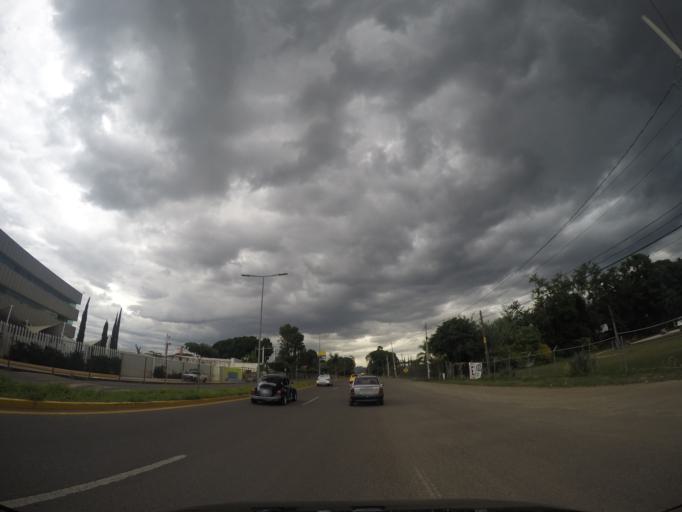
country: MX
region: Oaxaca
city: Tlalixtac de Cabrera
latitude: 17.0559
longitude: -96.6542
